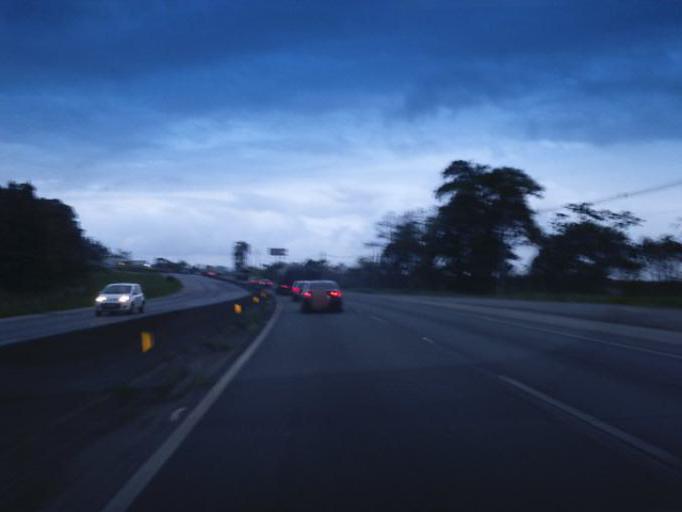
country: BR
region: Santa Catarina
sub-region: Joinville
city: Joinville
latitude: -26.4621
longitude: -48.7547
